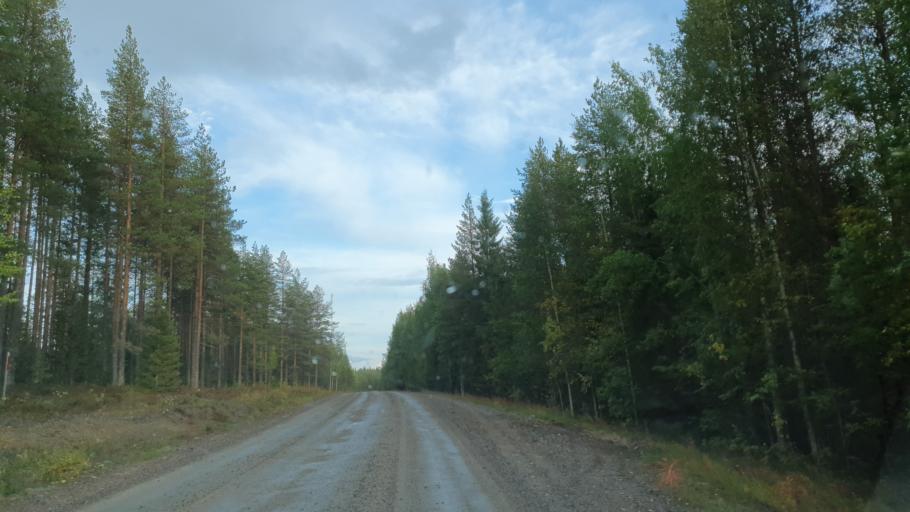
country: FI
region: Kainuu
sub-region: Kehys-Kainuu
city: Kuhmo
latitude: 64.4158
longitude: 29.5089
